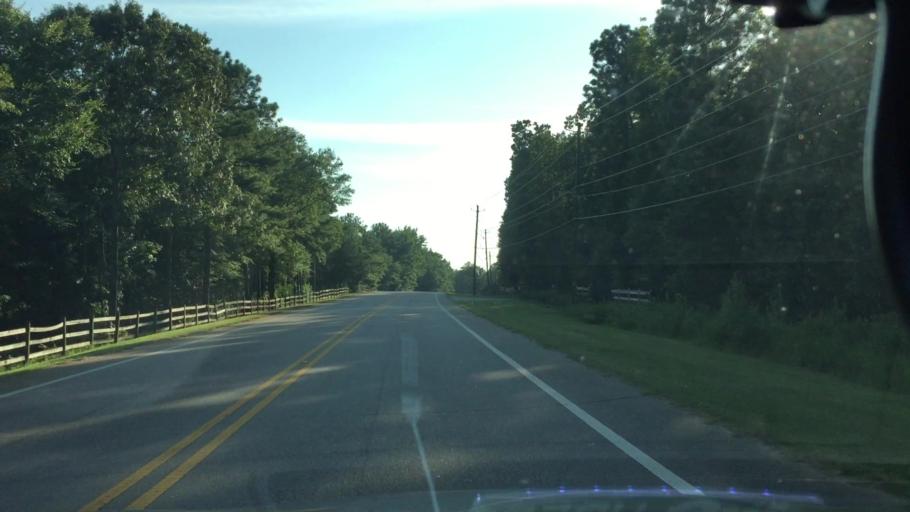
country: US
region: Alabama
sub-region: Lee County
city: Auburn
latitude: 32.5952
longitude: -85.4268
